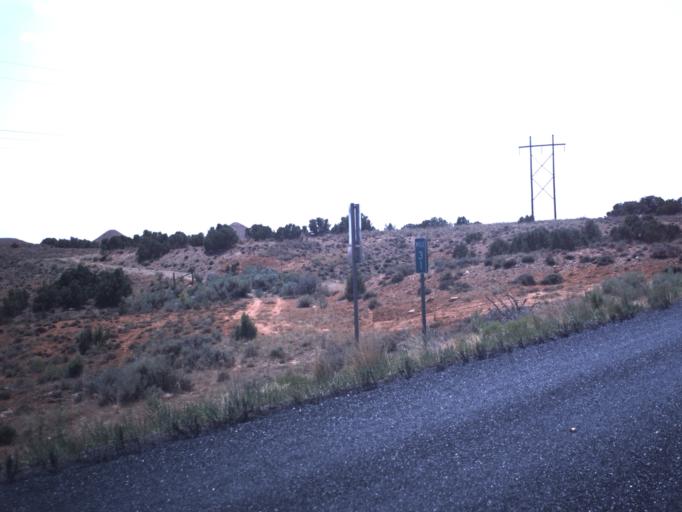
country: US
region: Utah
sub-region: Uintah County
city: Maeser
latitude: 40.4171
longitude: -109.6788
